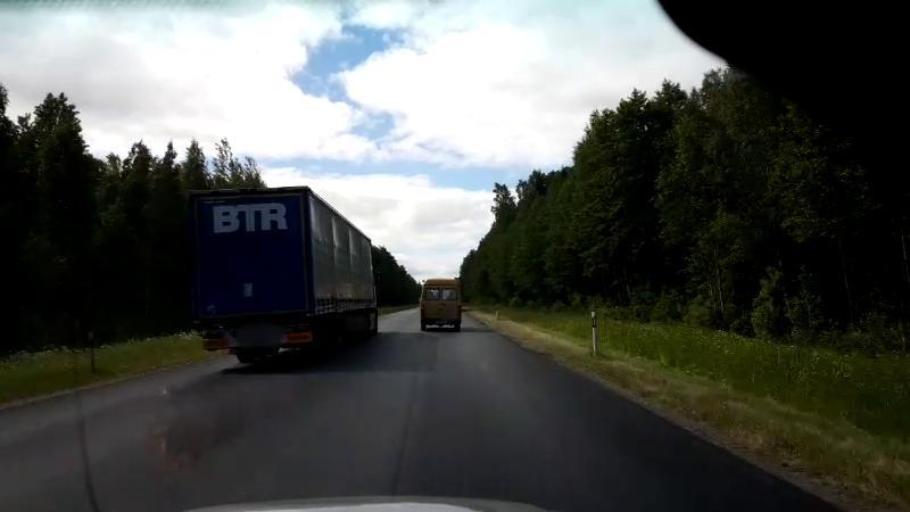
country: LV
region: Salacgrivas
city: Ainazi
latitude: 57.9543
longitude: 24.4395
